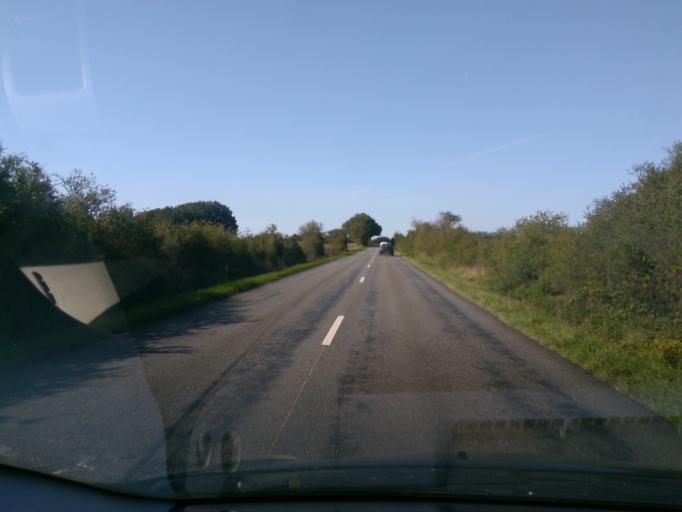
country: FR
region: Pays de la Loire
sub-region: Departement de la Loire-Atlantique
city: Quilly
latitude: 47.4648
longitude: -1.9231
